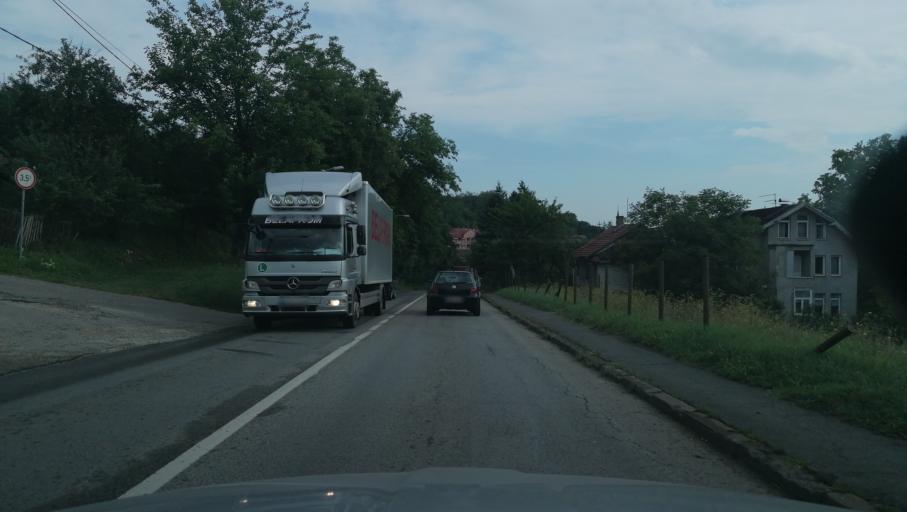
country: BA
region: Republika Srpska
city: Hiseti
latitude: 44.7637
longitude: 17.1760
